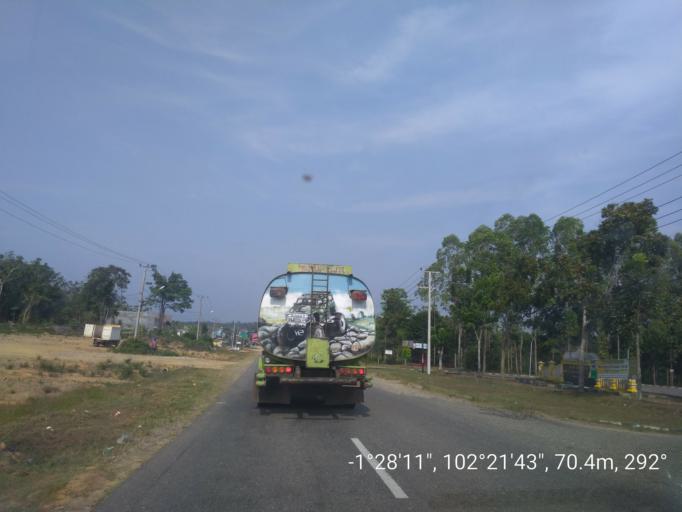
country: ID
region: Jambi
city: Muara Tebo
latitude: -1.4699
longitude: 102.3621
